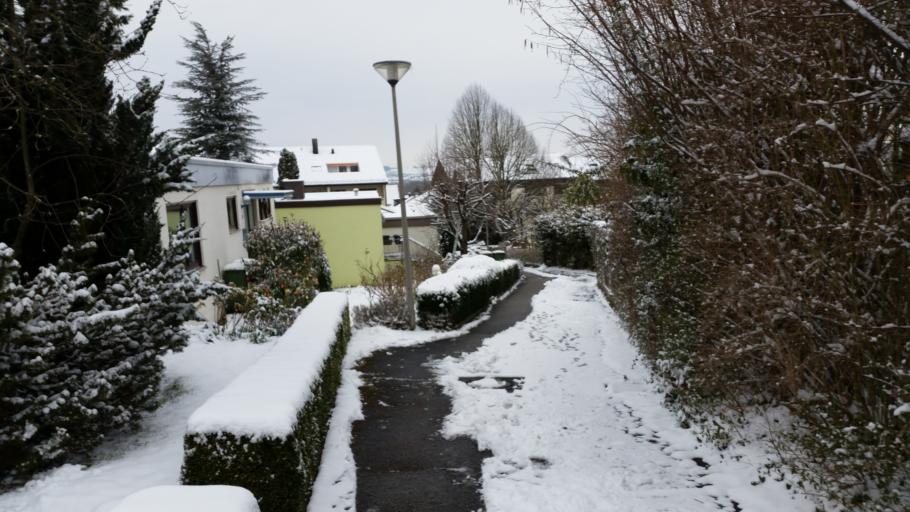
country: DE
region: Baden-Wuerttemberg
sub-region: Regierungsbezirk Stuttgart
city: Freiberg am Neckar
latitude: 48.9338
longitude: 9.2069
